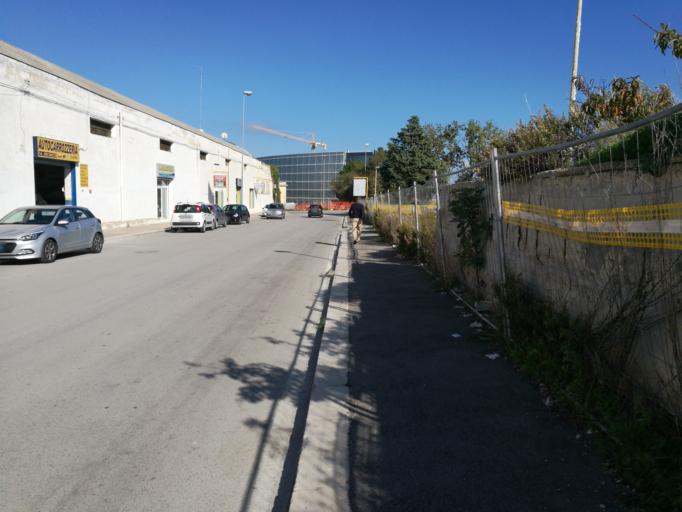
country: IT
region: Apulia
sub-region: Provincia di Bari
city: Triggiano
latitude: 41.1068
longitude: 16.9120
